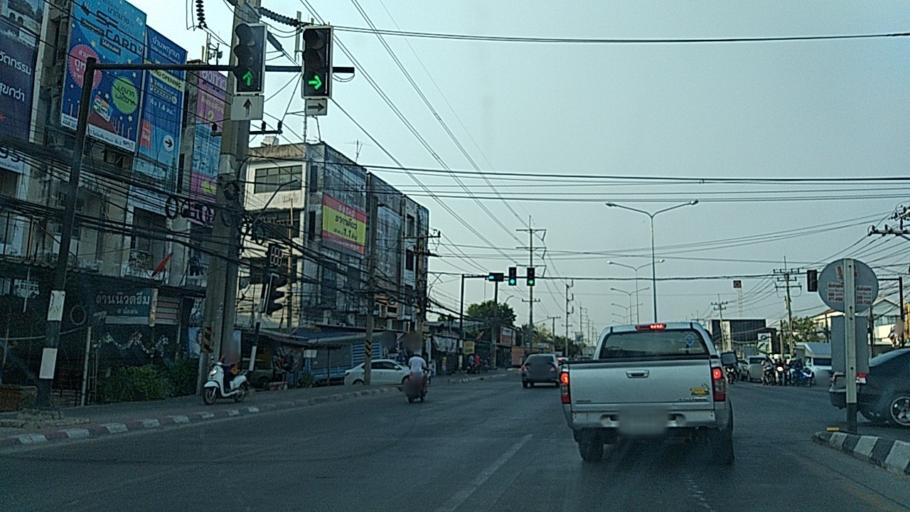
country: TH
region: Phra Nakhon Si Ayutthaya
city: Ban Bang Kadi Pathum Thani
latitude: 13.9822
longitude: 100.5506
